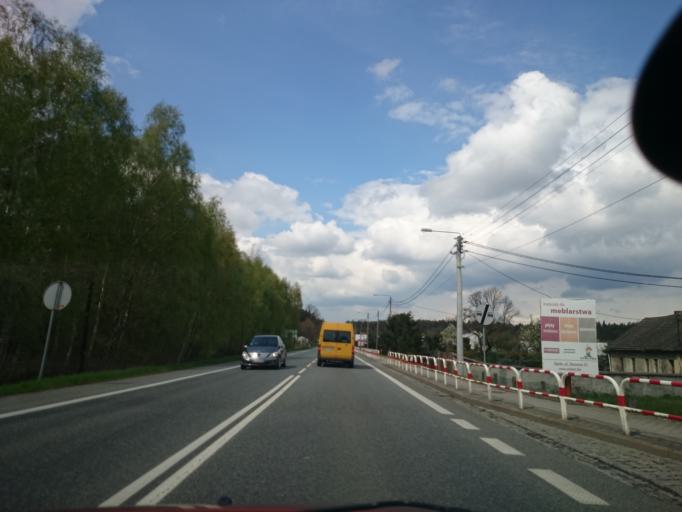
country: PL
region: Opole Voivodeship
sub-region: Powiat opolski
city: Tarnow Opolski
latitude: 50.6076
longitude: 18.0723
